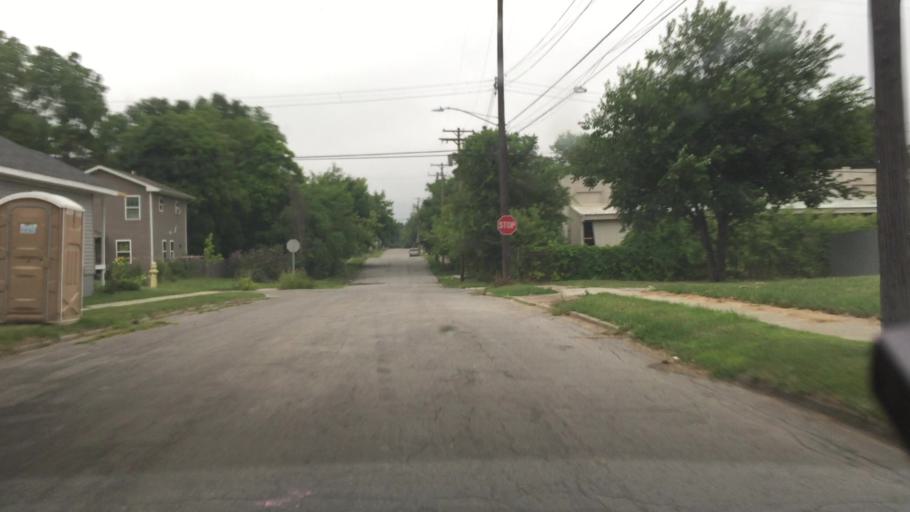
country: US
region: Michigan
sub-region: Oakland County
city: Pontiac
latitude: 42.6222
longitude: -83.2725
